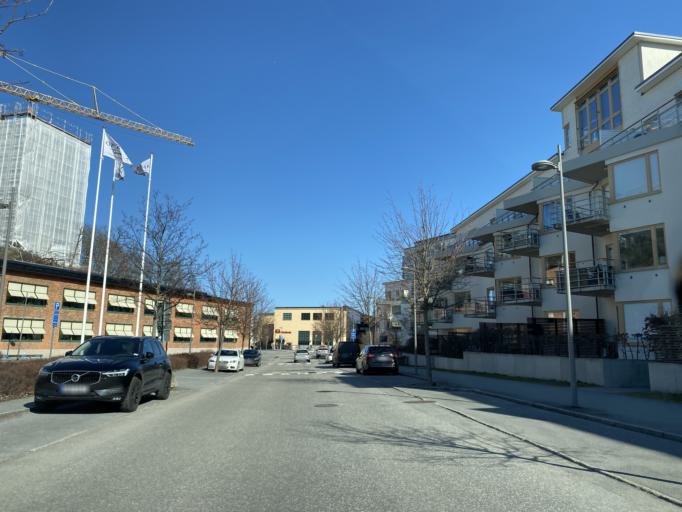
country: SE
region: Stockholm
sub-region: Nacka Kommun
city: Nacka
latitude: 59.3138
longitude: 18.1222
